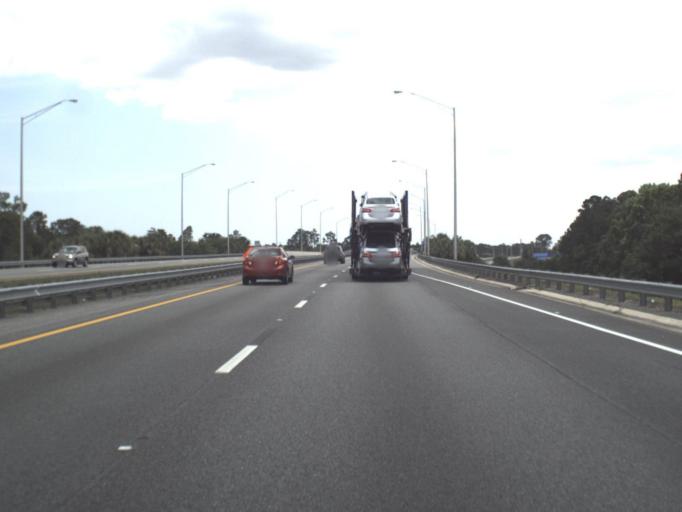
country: US
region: Florida
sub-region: Duval County
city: Atlantic Beach
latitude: 30.3192
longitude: -81.5258
